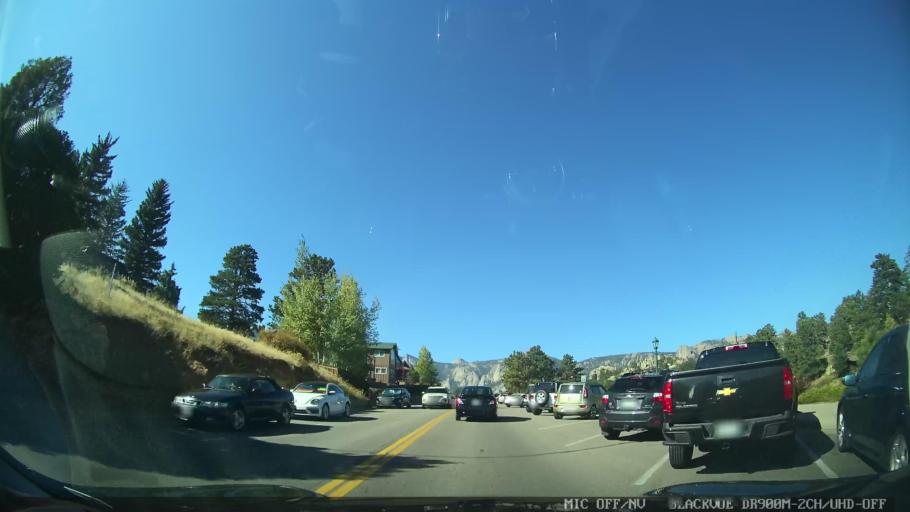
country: US
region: Colorado
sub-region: Larimer County
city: Estes Park
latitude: 40.3785
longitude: -105.5214
